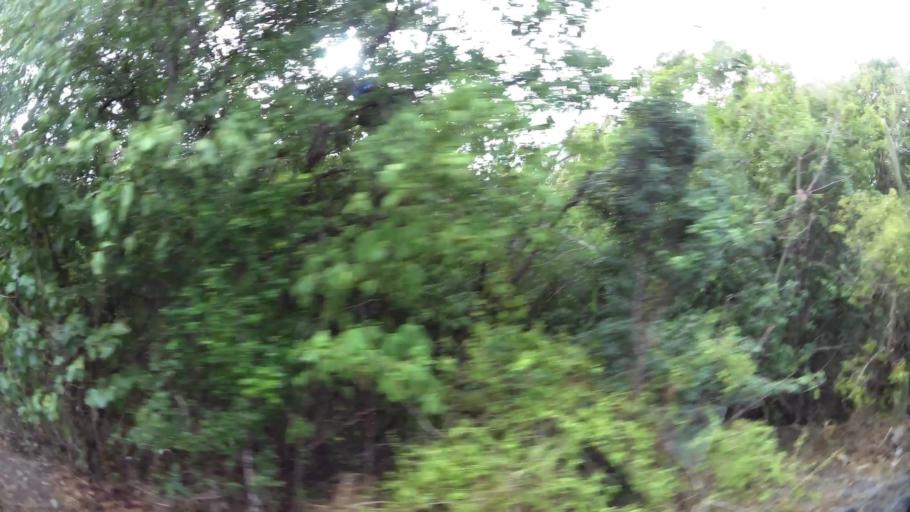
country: KN
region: Saint James Windwa
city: Newcastle
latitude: 17.1997
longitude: -62.5972
